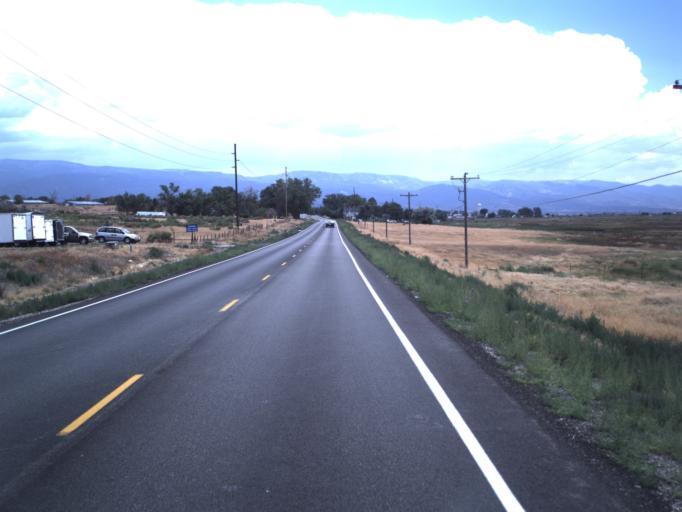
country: US
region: Utah
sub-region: Sanpete County
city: Moroni
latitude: 39.5404
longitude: -111.5951
